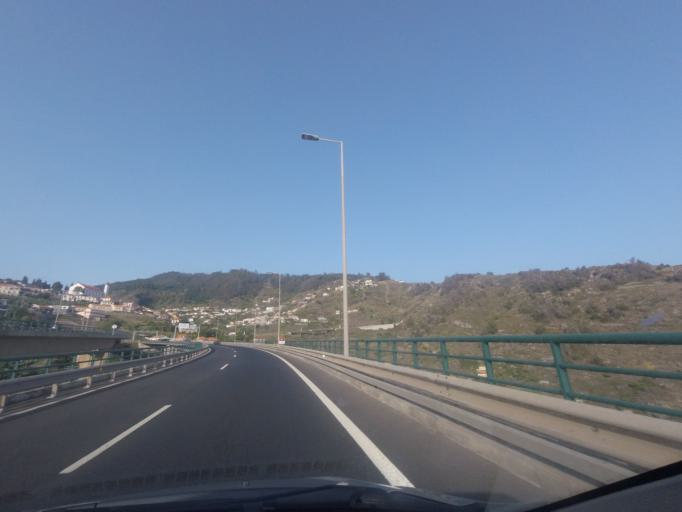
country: PT
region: Madeira
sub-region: Ribeira Brava
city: Campanario
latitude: 32.6651
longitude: -17.0349
